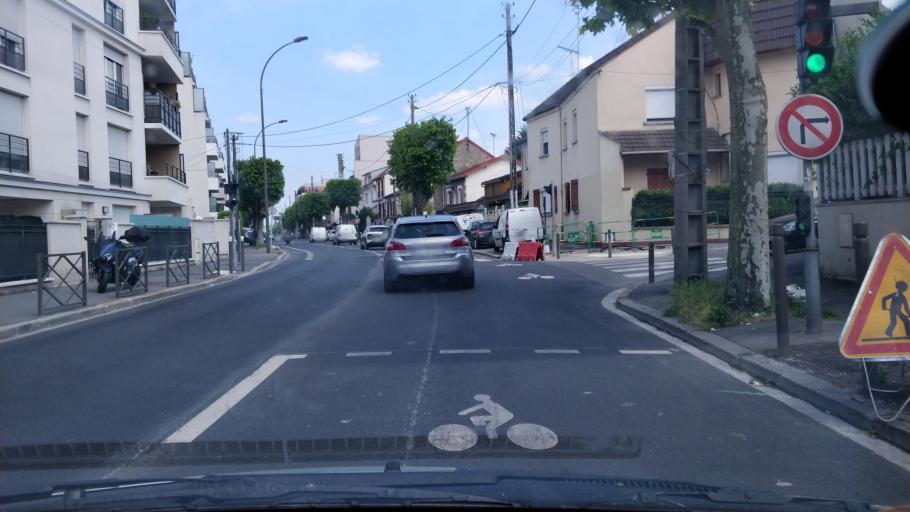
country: FR
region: Ile-de-France
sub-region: Departement de Seine-Saint-Denis
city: Villemomble
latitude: 48.8785
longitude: 2.4895
